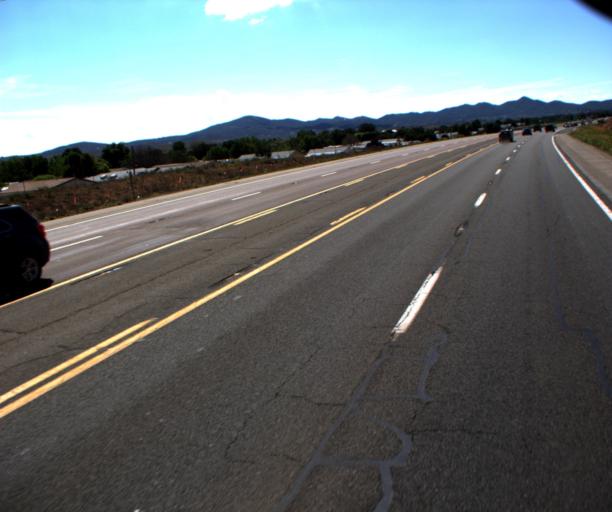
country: US
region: Arizona
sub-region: Yavapai County
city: Dewey-Humboldt
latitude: 34.5572
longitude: -112.2553
